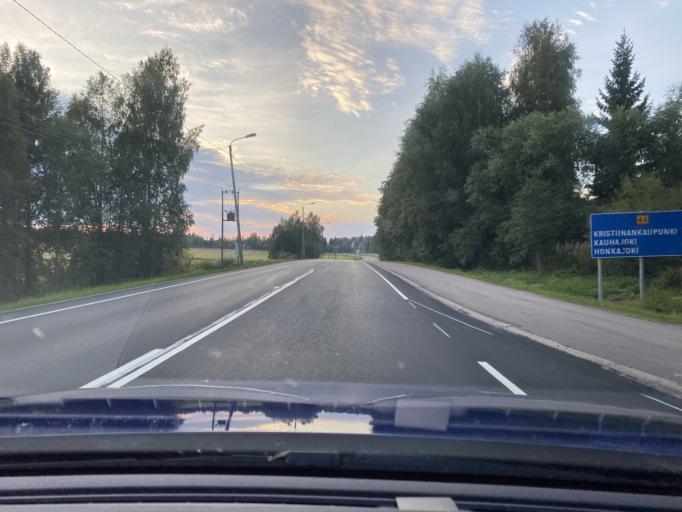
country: FI
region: Satakunta
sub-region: Pohjois-Satakunta
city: Kankaanpaeae
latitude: 61.8232
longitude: 22.3628
